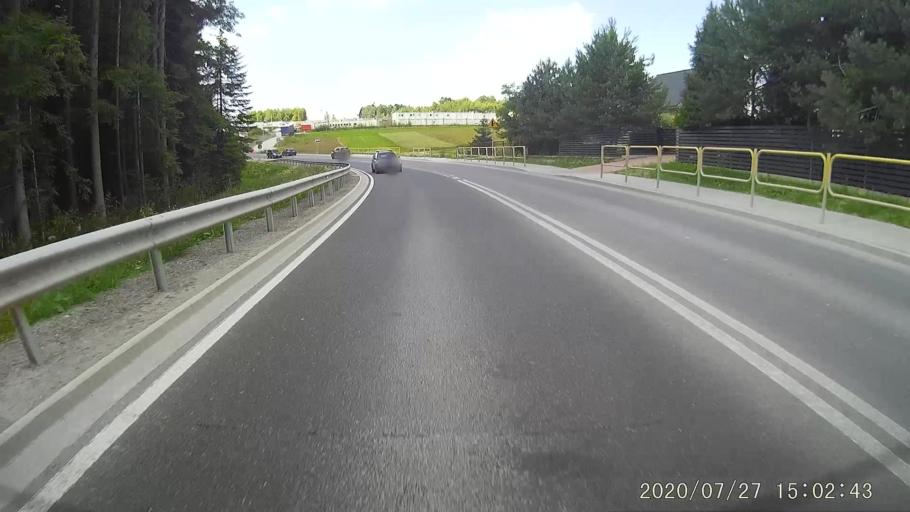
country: PL
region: Lesser Poland Voivodeship
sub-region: Powiat suski
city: Naprawa
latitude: 49.6715
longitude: 19.8913
